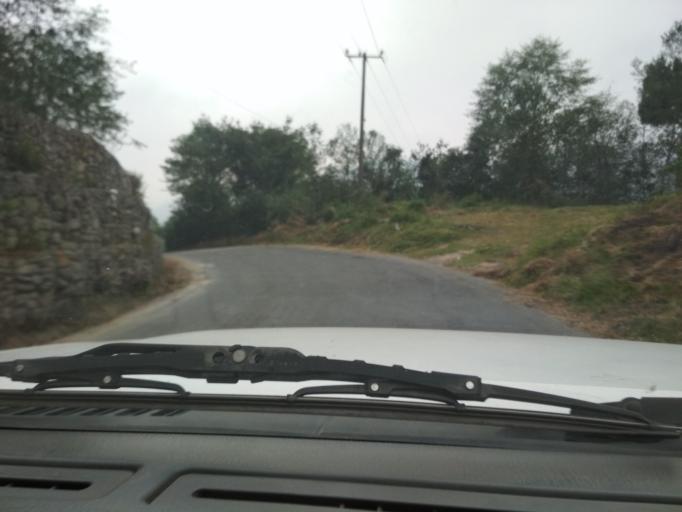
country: MX
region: Veracruz
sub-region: La Perla
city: Metlac Hernandez (Metlac Primero)
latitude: 18.9624
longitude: -97.1476
